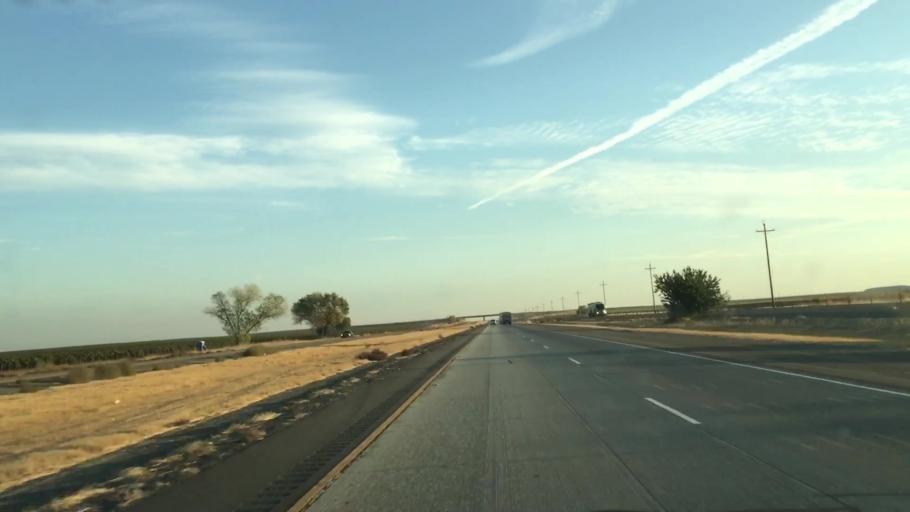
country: US
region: California
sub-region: Yolo County
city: Esparto
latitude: 38.7396
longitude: -121.9546
